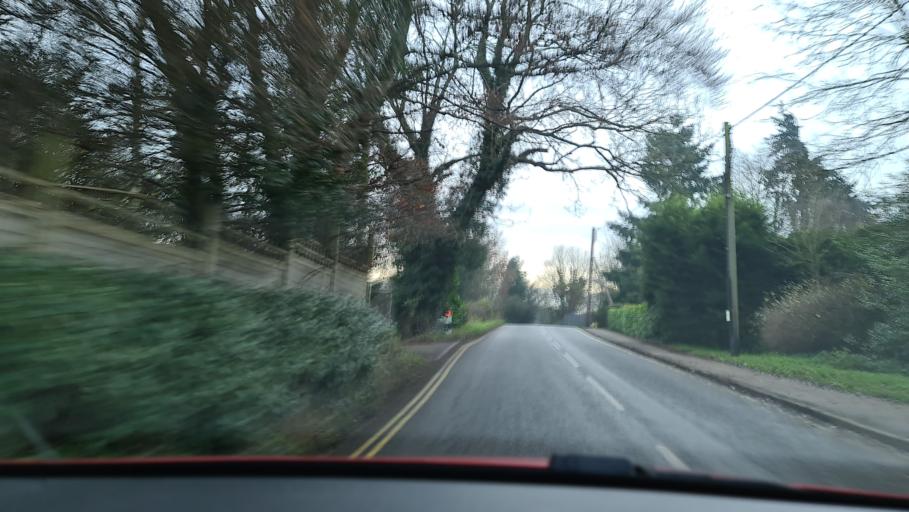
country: GB
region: England
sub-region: Buckinghamshire
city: Great Missenden
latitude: 51.7073
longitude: -0.7130
